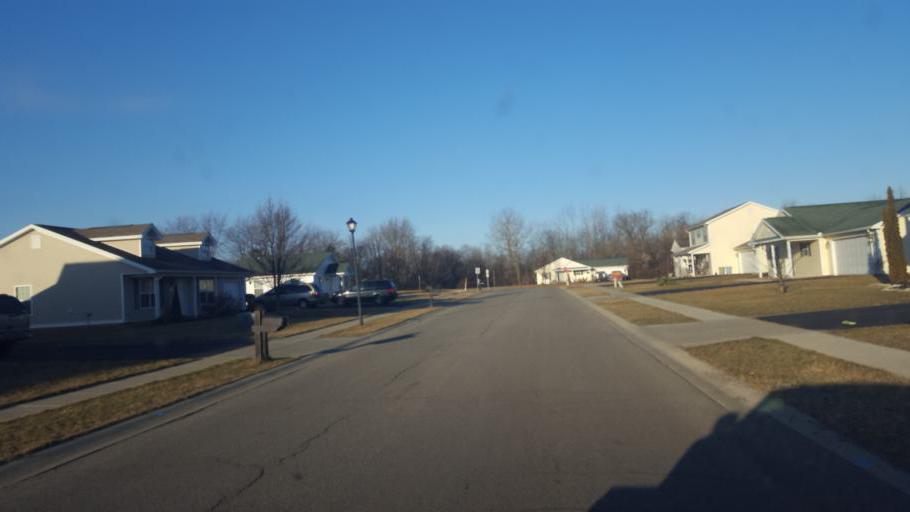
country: US
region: Ohio
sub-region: Morrow County
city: Mount Gilead
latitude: 40.5534
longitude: -82.8470
